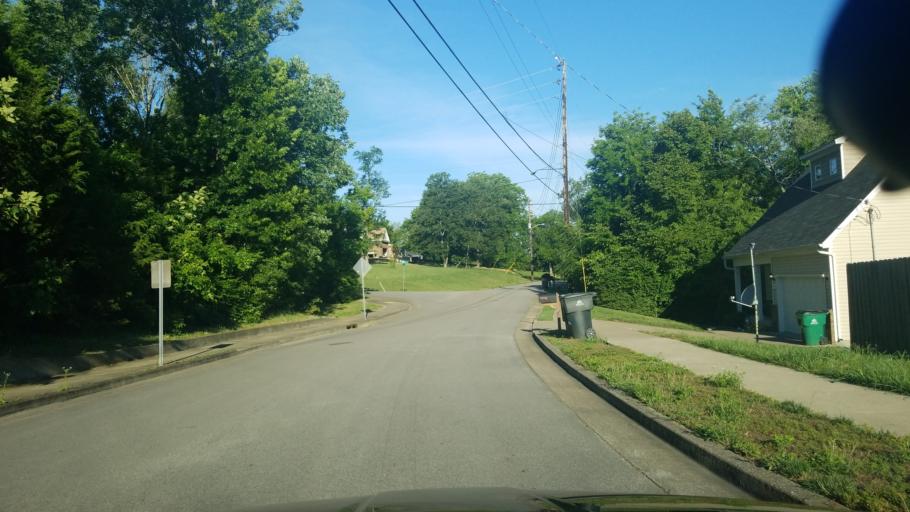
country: US
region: Tennessee
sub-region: Davidson County
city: Nashville
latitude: 36.2398
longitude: -86.7625
